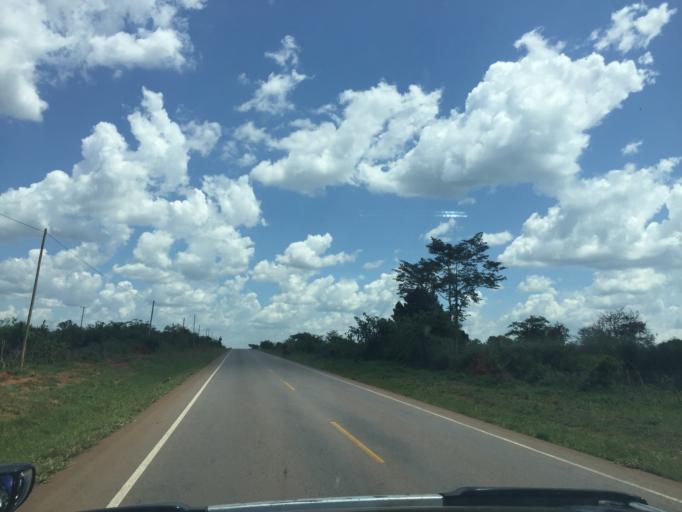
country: UG
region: Central Region
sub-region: Nakasongola District
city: Nakasongola
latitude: 1.3706
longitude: 32.3534
